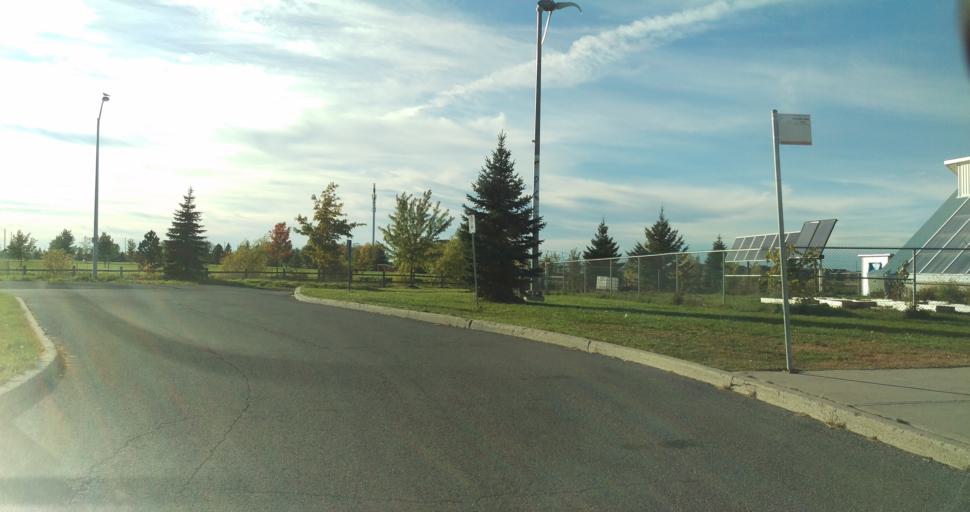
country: CA
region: Ontario
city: Clarence-Rockland
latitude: 45.4685
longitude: -75.4461
